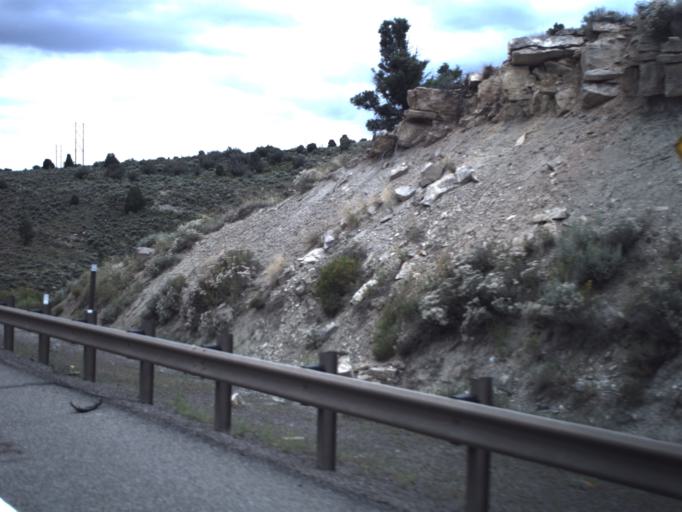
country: US
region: Utah
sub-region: Carbon County
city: Helper
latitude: 39.8268
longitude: -110.9542
